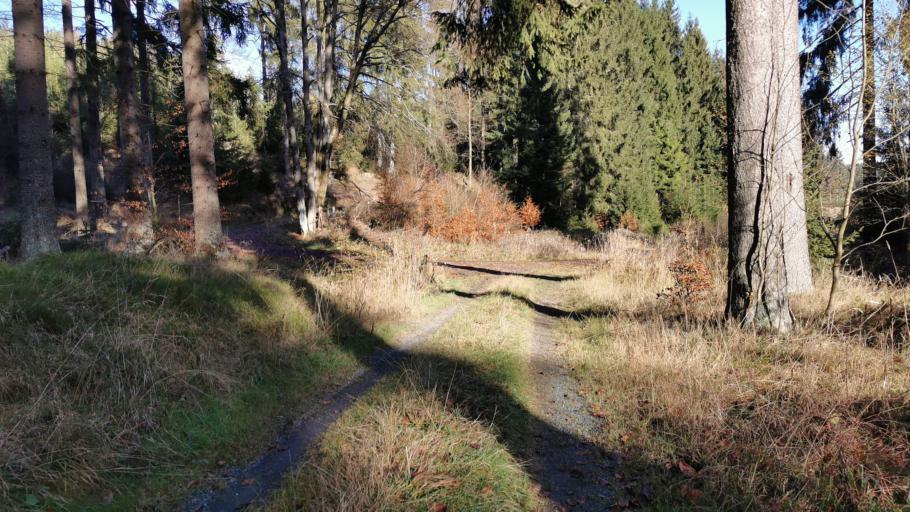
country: DE
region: Bavaria
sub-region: Upper Franconia
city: Reichenbach
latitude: 50.4480
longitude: 11.4292
